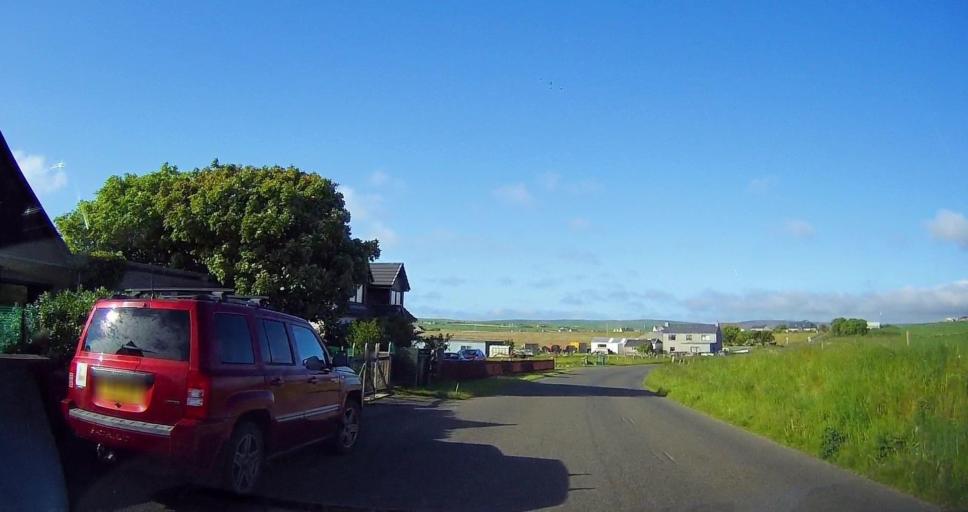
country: GB
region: Scotland
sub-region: Orkney Islands
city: Stromness
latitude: 59.0708
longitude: -3.2269
